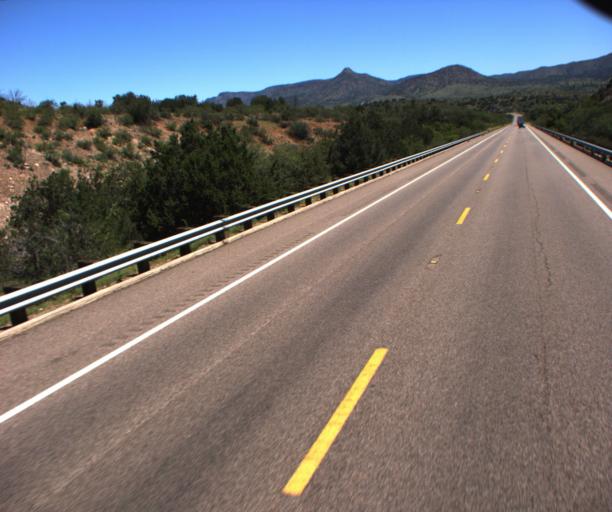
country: US
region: Arizona
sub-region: Gila County
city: Globe
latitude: 33.5708
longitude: -110.6628
